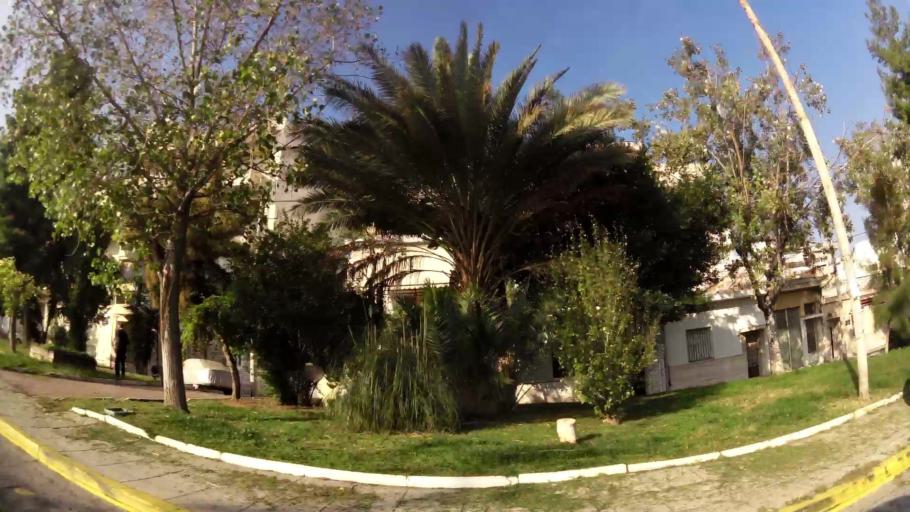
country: GR
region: Attica
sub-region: Nomos Piraios
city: Drapetsona
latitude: 37.9544
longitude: 23.6228
